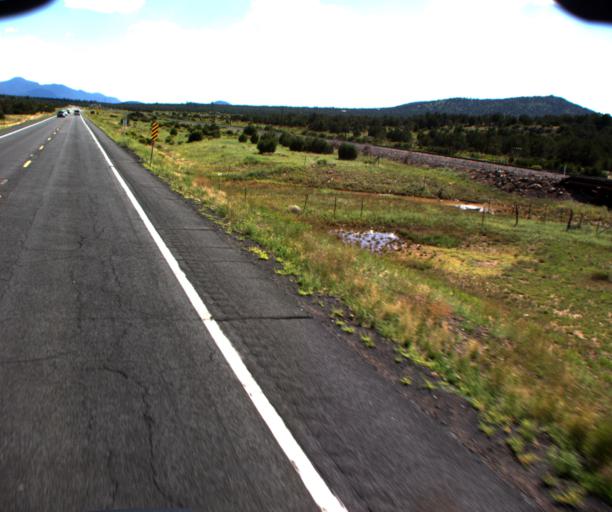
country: US
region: Arizona
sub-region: Coconino County
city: Williams
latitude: 35.3737
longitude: -112.1628
